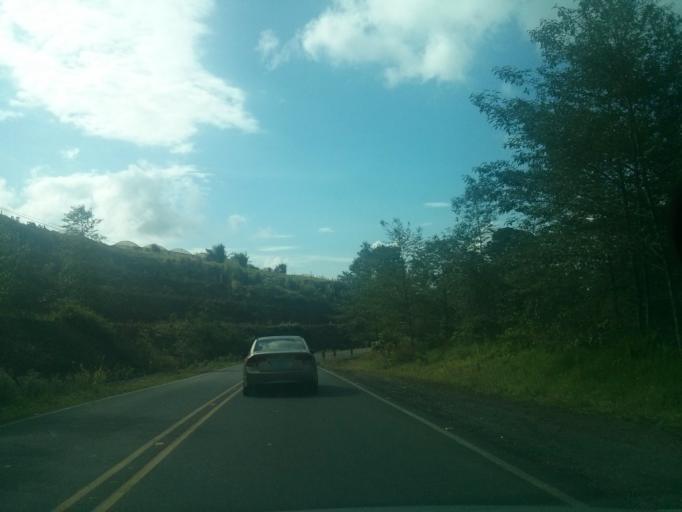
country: CR
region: Heredia
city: Santo Domingo
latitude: 10.1896
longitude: -84.1537
